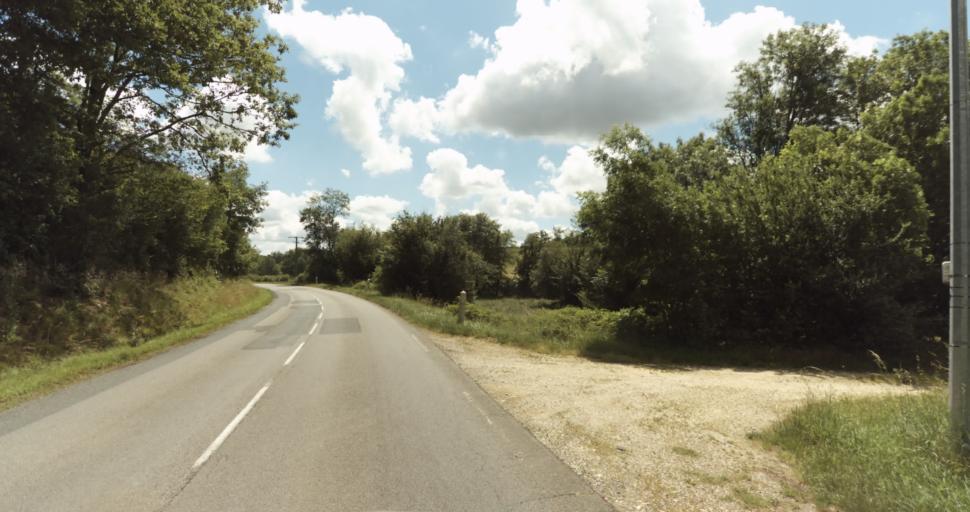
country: FR
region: Aquitaine
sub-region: Departement de la Dordogne
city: Lalinde
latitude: 44.7979
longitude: 0.7414
